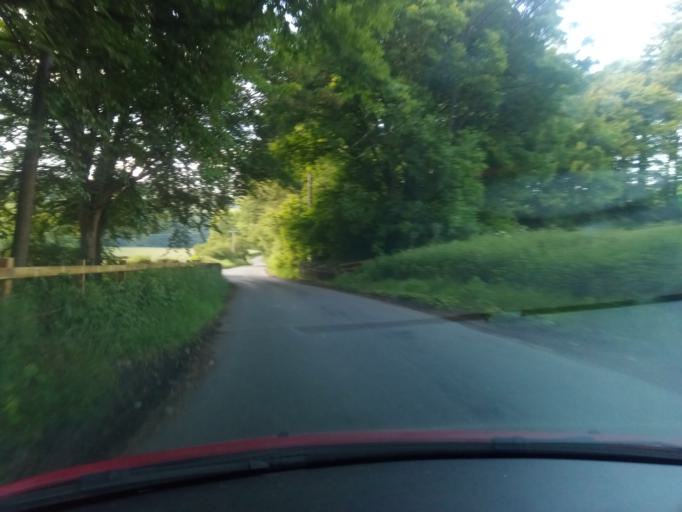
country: GB
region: Scotland
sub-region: The Scottish Borders
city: Selkirk
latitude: 55.5180
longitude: -2.9237
